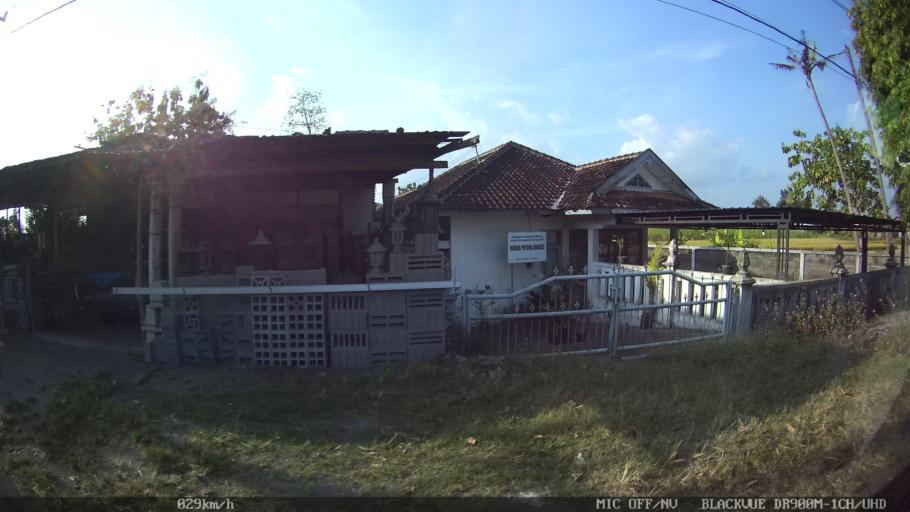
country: ID
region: Daerah Istimewa Yogyakarta
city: Sewon
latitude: -7.8674
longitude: 110.3478
